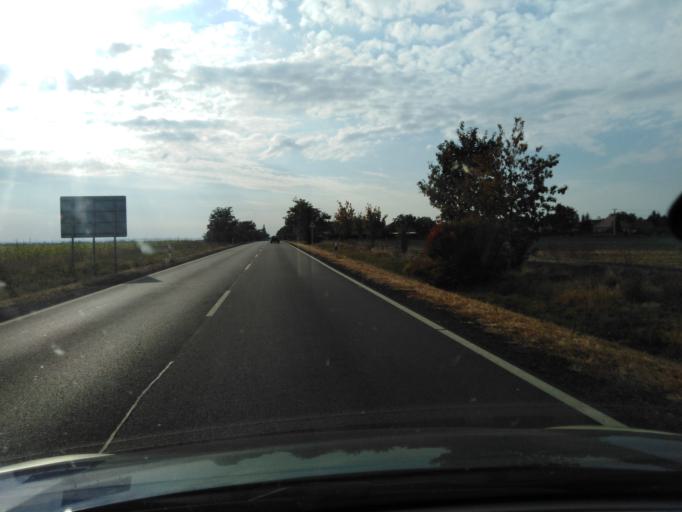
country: HU
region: Heves
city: Hered
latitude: 47.6604
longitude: 19.6341
